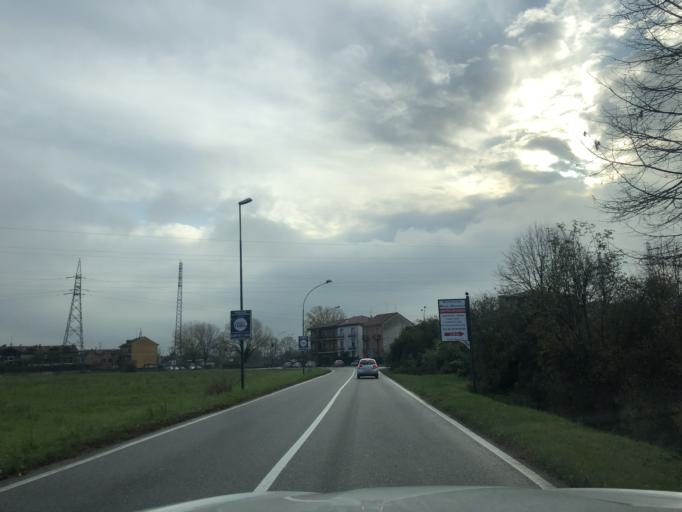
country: IT
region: Lombardy
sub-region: Citta metropolitana di Milano
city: Cologno Monzese
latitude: 45.5492
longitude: 9.2720
